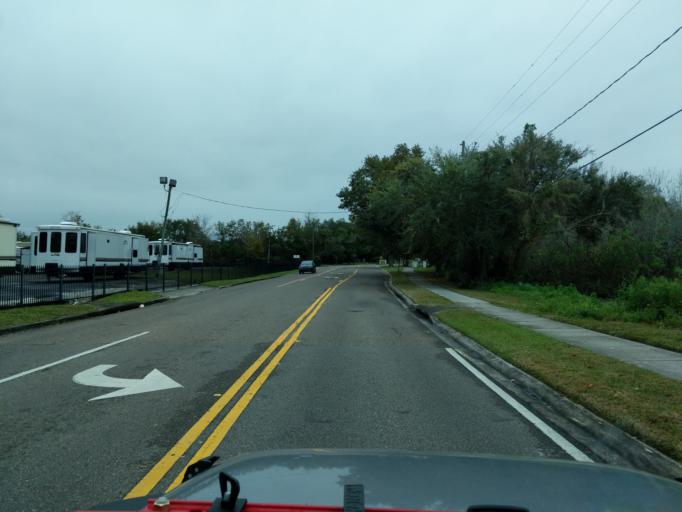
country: US
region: Florida
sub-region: Orange County
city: Winter Garden
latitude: 28.5506
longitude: -81.5918
